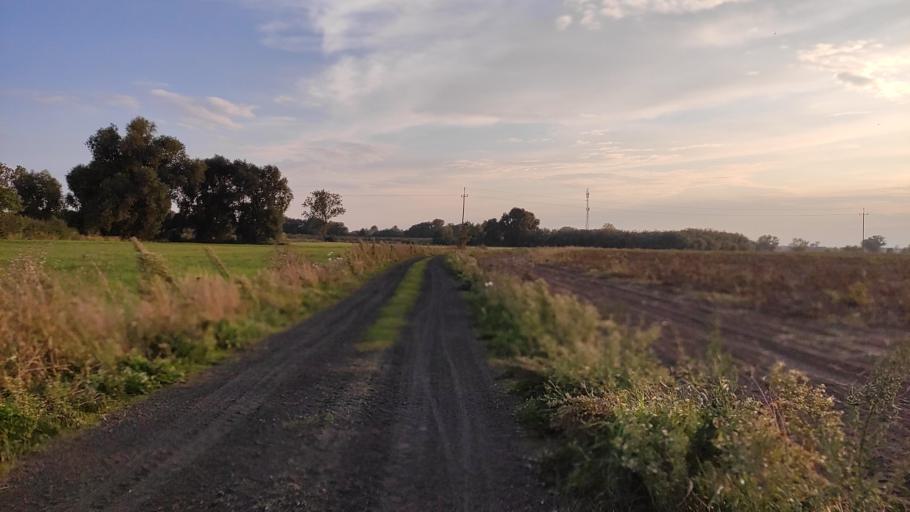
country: PL
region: Greater Poland Voivodeship
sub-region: Powiat poznanski
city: Kostrzyn
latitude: 52.3903
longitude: 17.1784
